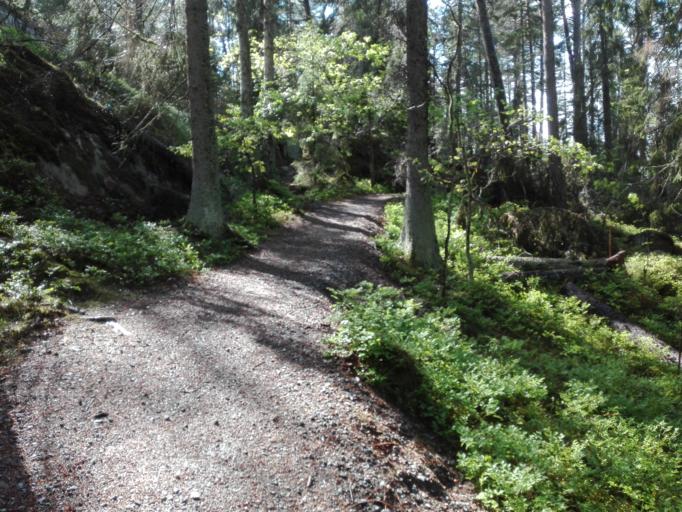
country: SE
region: Stockholm
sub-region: Nacka Kommun
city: Fisksatra
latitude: 59.2957
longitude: 18.2727
